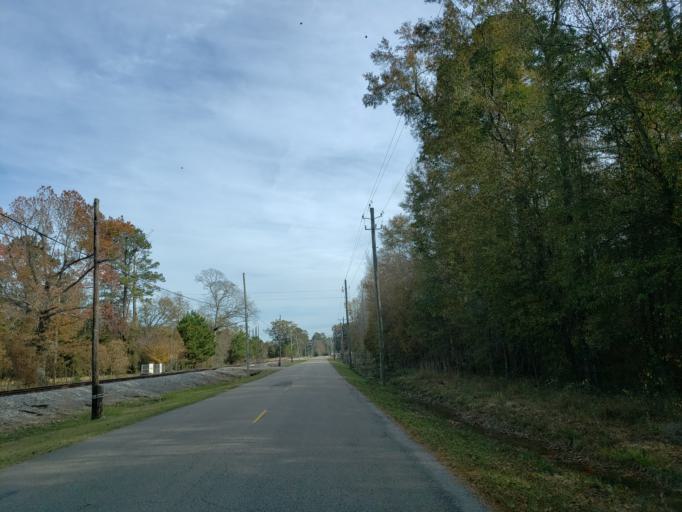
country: US
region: Mississippi
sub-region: Forrest County
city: Glendale
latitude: 31.3520
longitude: -89.3255
